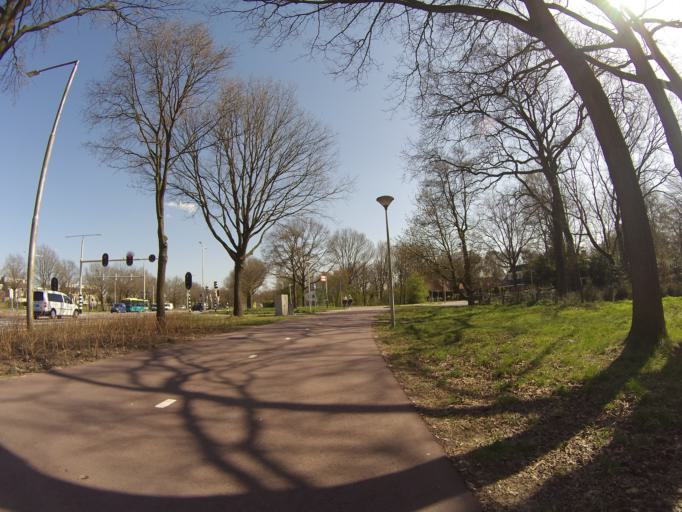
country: NL
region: Utrecht
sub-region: Gemeente Amersfoort
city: Hoogland
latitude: 52.1699
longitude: 5.3733
